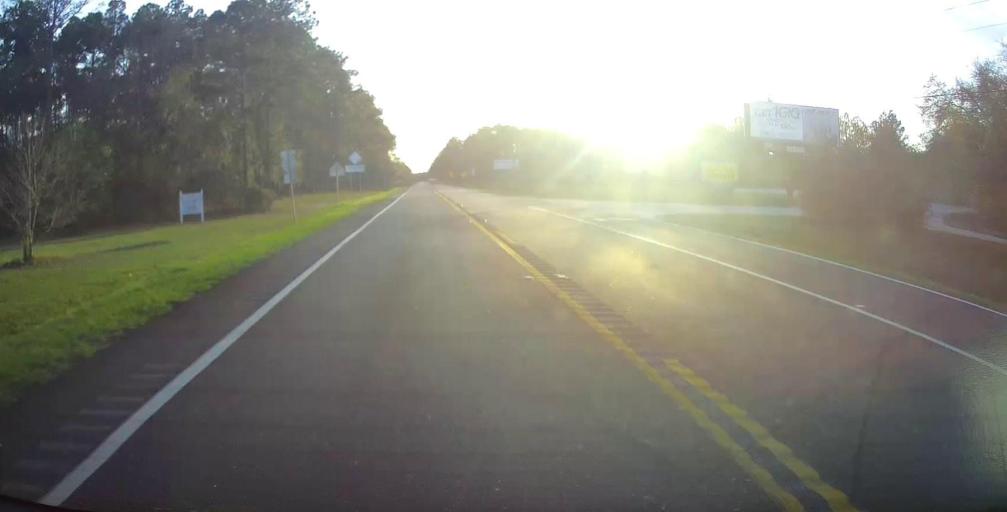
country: US
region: Georgia
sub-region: Bryan County
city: Pembroke
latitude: 32.1651
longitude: -81.4923
